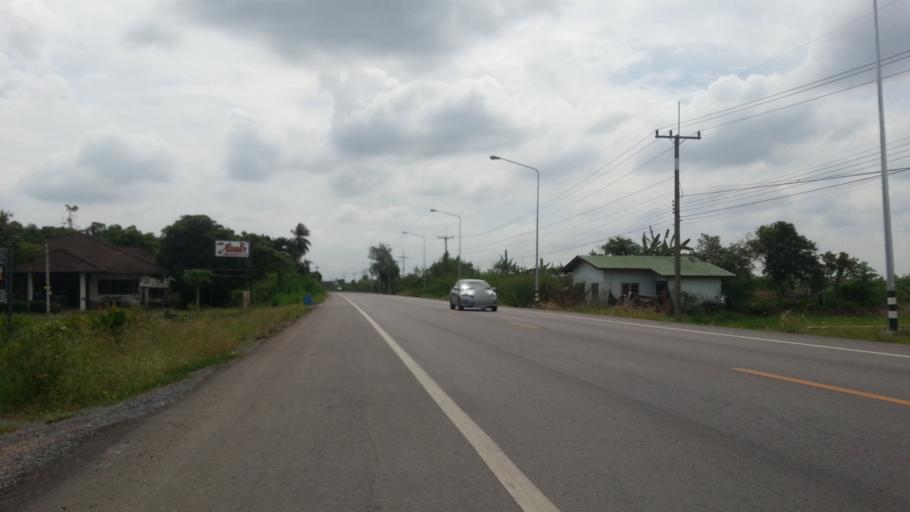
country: TH
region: Pathum Thani
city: Ban Rangsit
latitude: 14.0406
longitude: 100.8443
